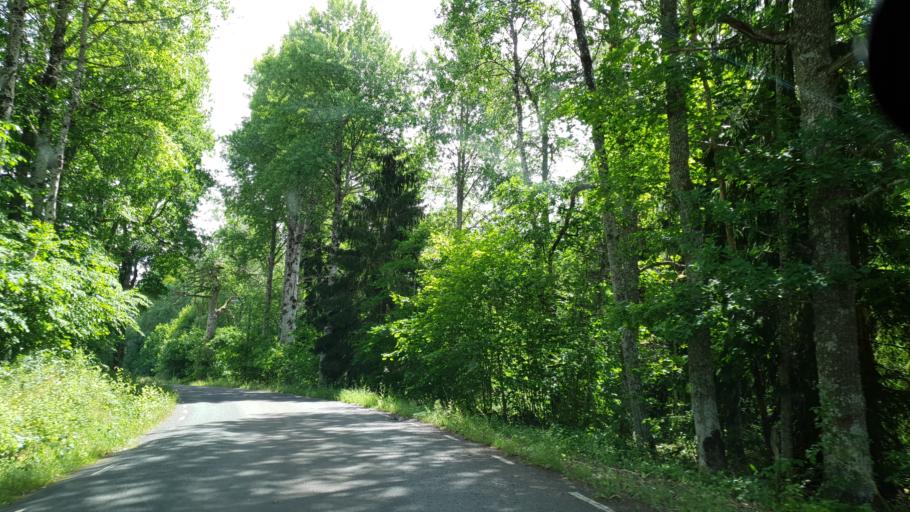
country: SE
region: Kalmar
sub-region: Hultsfreds Kommun
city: Virserum
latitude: 57.0999
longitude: 15.5830
